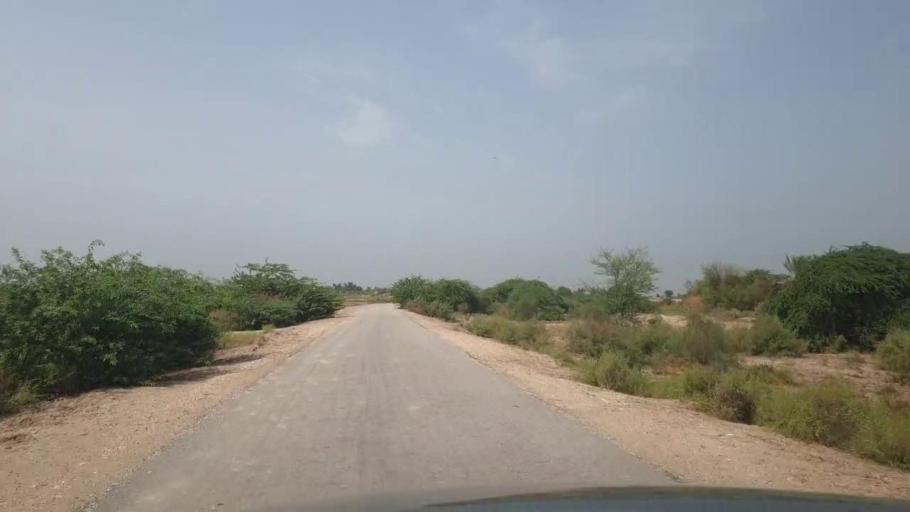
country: PK
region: Sindh
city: Madeji
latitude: 27.8387
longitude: 68.4311
